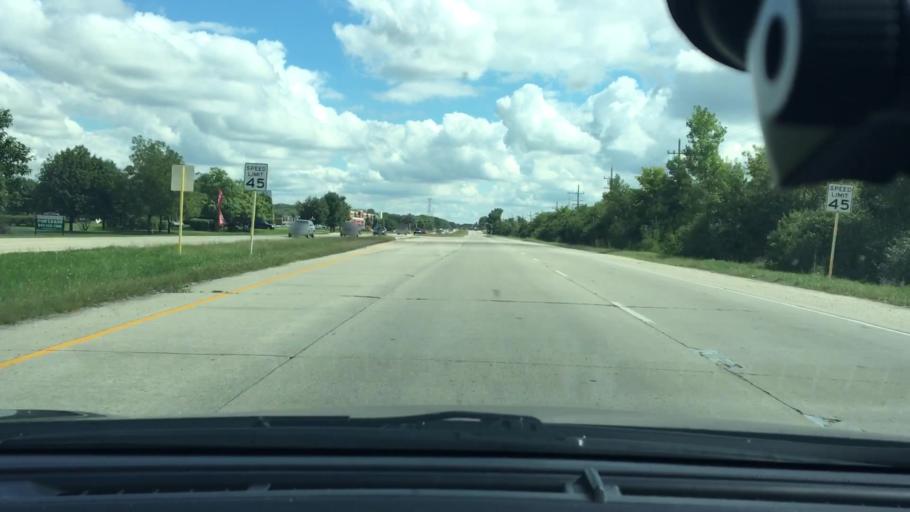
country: US
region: Illinois
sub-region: Kane County
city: East Dundee
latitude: 42.0900
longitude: -88.2497
